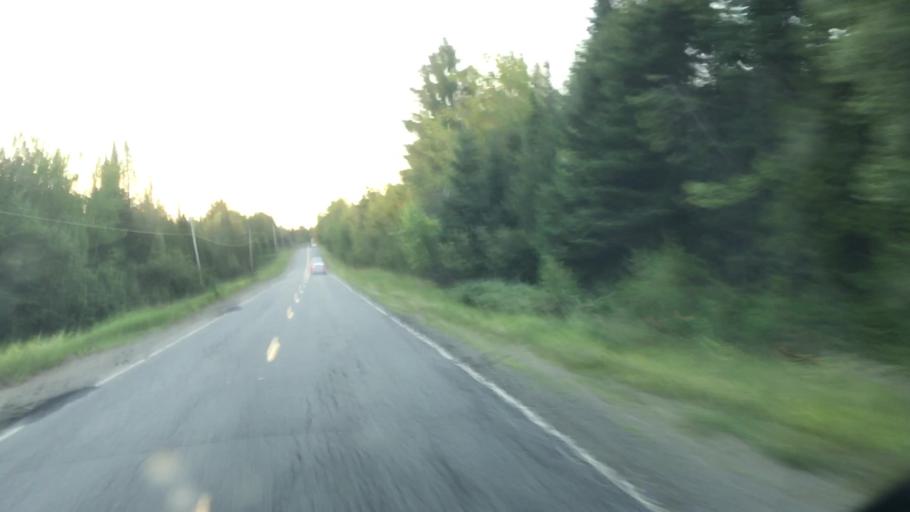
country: US
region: Maine
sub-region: Penobscot County
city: Medway
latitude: 45.6021
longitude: -68.2505
